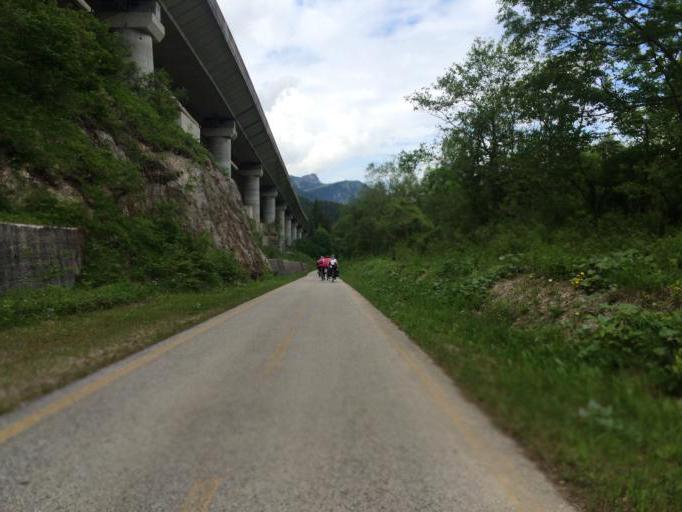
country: IT
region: Friuli Venezia Giulia
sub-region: Provincia di Udine
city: Malborghetto
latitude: 46.5043
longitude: 13.4472
